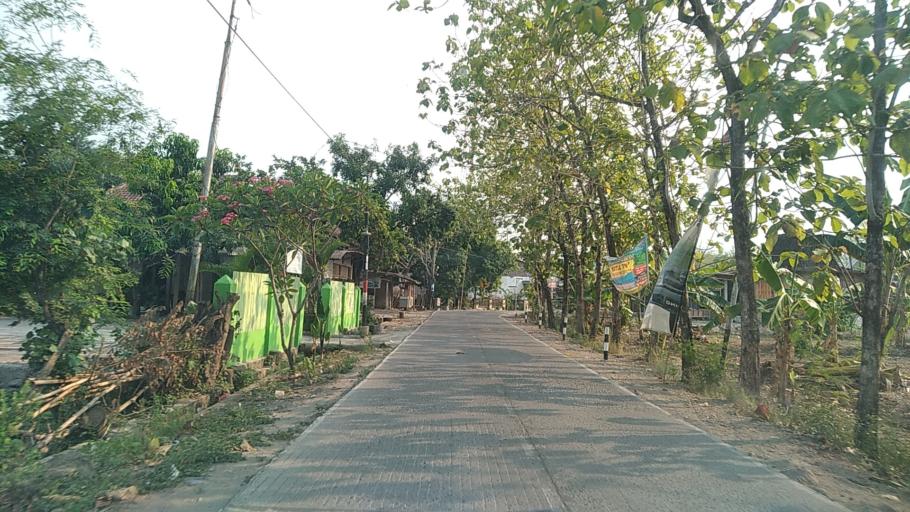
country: ID
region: Central Java
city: Mranggen
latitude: -7.0655
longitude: 110.4991
